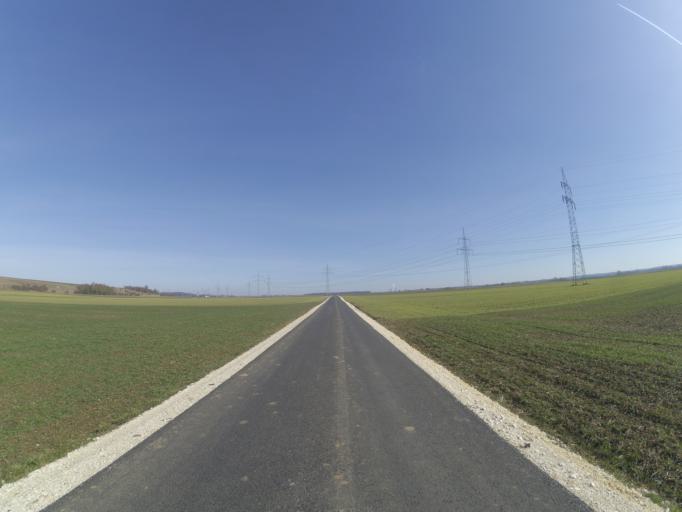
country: DE
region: Baden-Wuerttemberg
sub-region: Tuebingen Region
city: Asselfingen
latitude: 48.5145
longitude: 10.2114
